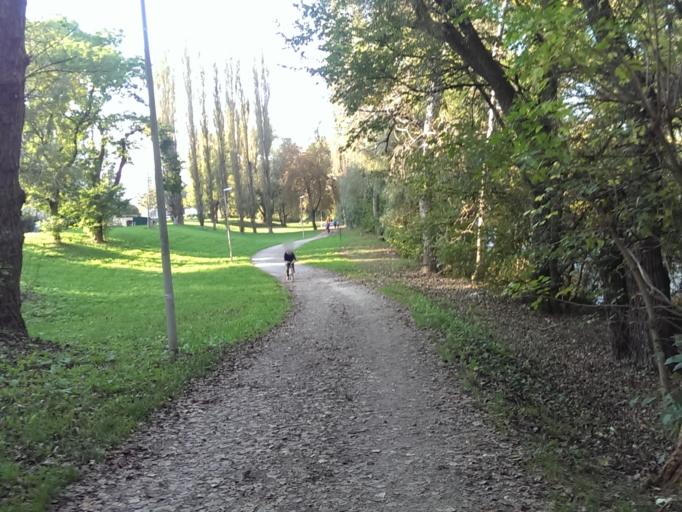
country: AT
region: Styria
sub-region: Graz Stadt
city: Goesting
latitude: 47.0955
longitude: 15.4163
